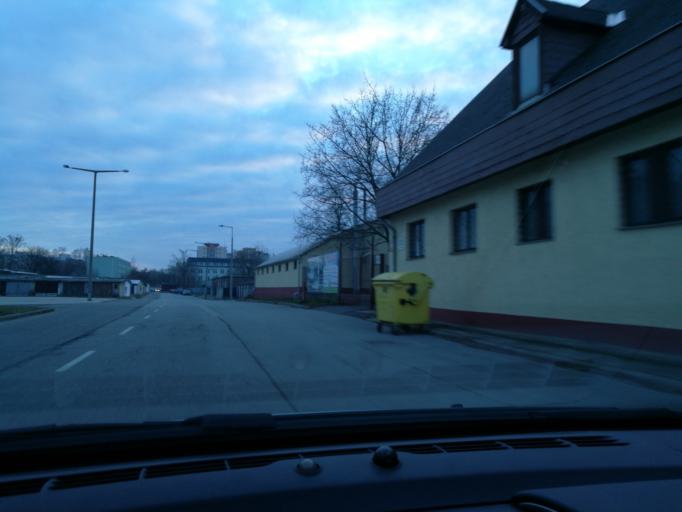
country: HU
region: Szabolcs-Szatmar-Bereg
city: Nyiregyhaza
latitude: 47.9712
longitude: 21.7115
